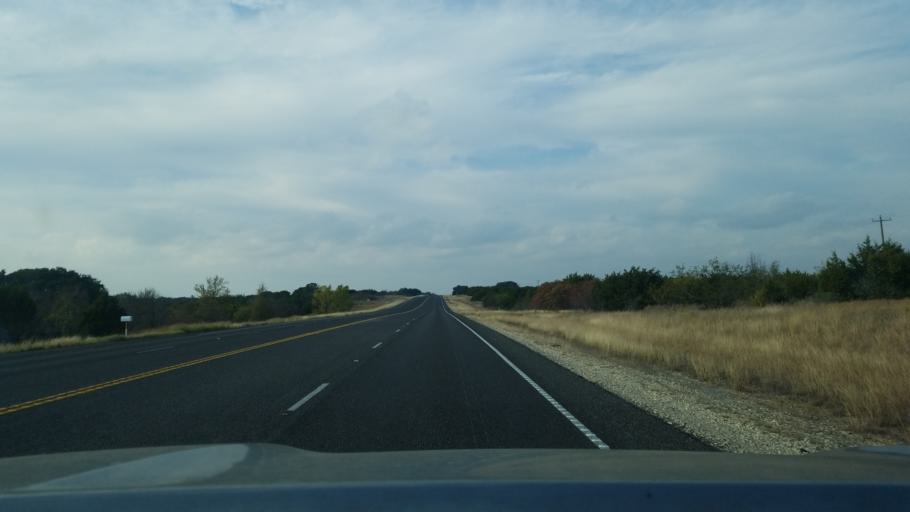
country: US
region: Texas
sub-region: Mills County
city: Goldthwaite
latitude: 31.3096
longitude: -98.4806
